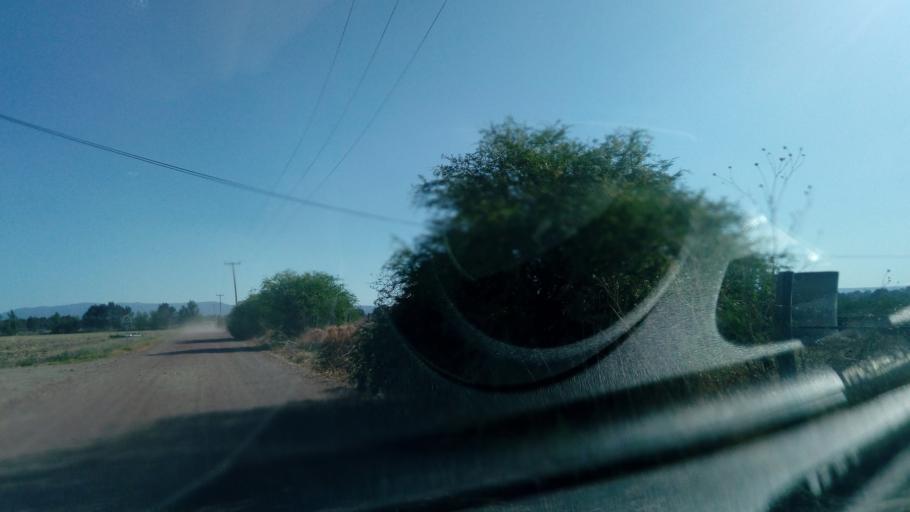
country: MX
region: Durango
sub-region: Durango
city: Jose Refugio Salcido
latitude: 24.0161
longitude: -104.5536
